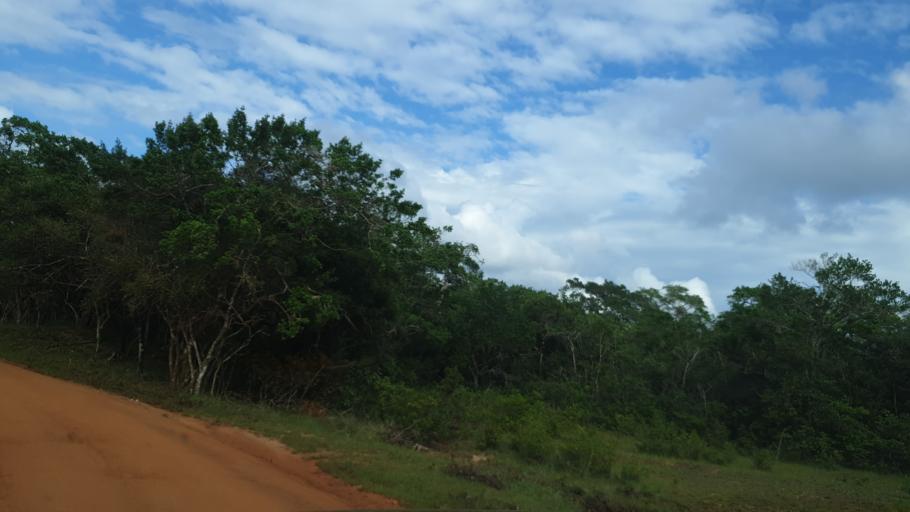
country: LK
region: North Central
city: Anuradhapura
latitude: 8.3618
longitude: 80.0957
